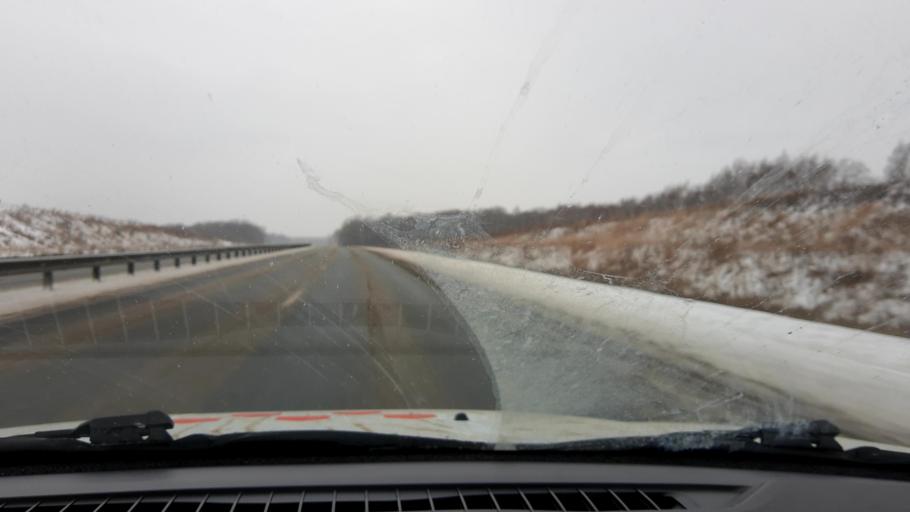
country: RU
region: Nizjnij Novgorod
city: Kstovo
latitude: 56.1005
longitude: 44.0483
